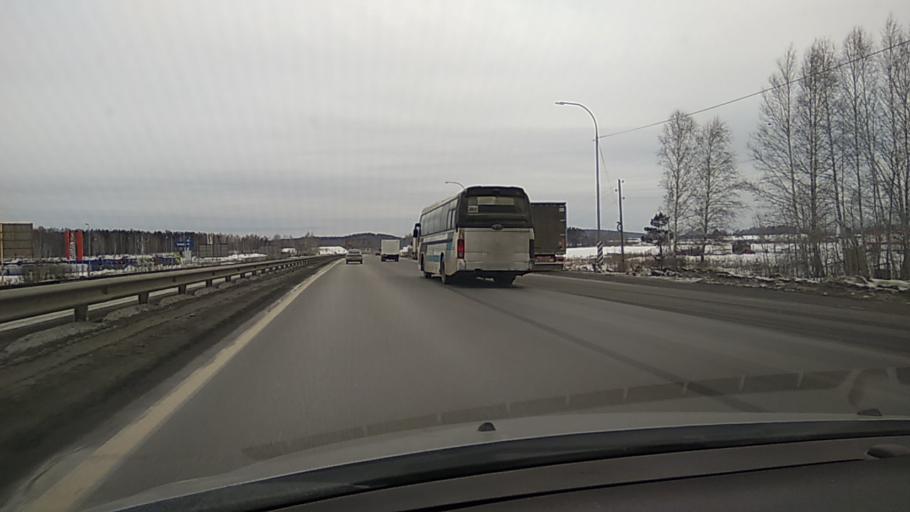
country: RU
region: Sverdlovsk
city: Talitsa
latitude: 56.8377
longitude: 60.1581
